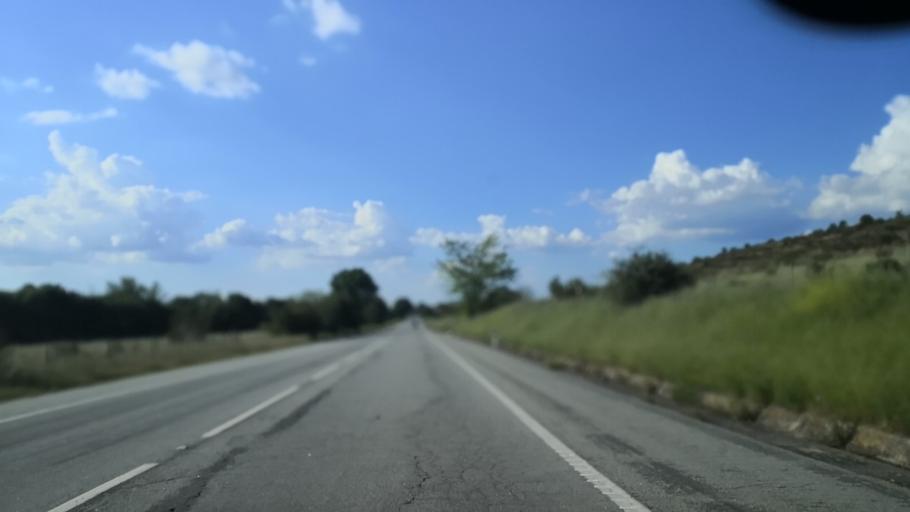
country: PT
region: Portalegre
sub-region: Portalegre
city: Urra
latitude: 39.0792
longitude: -7.4365
